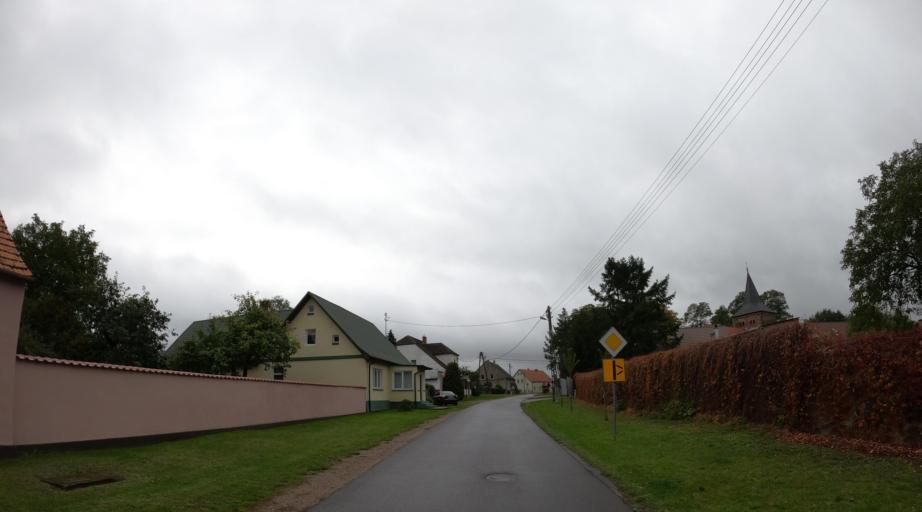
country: PL
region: West Pomeranian Voivodeship
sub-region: Powiat gryfinski
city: Gryfino
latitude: 53.2582
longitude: 14.5786
